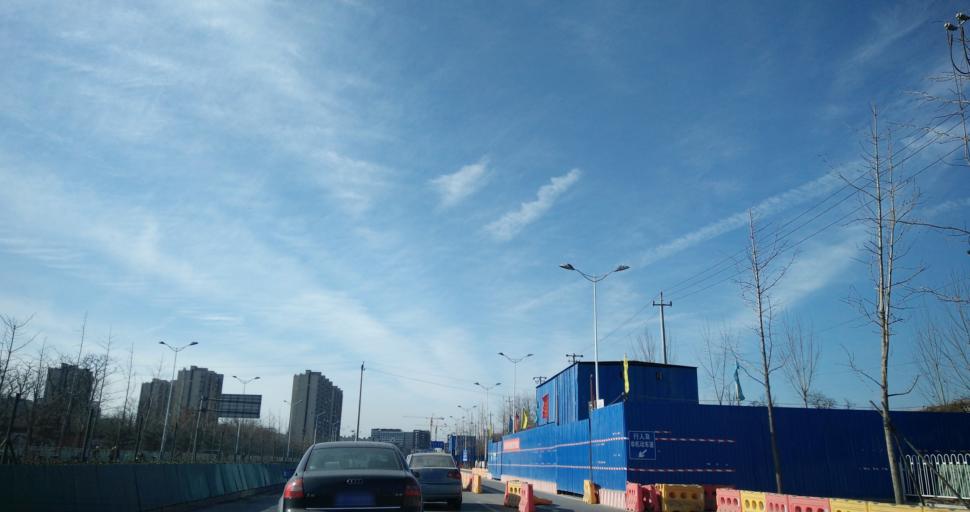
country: CN
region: Beijing
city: Xingfeng
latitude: 39.7418
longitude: 116.3477
